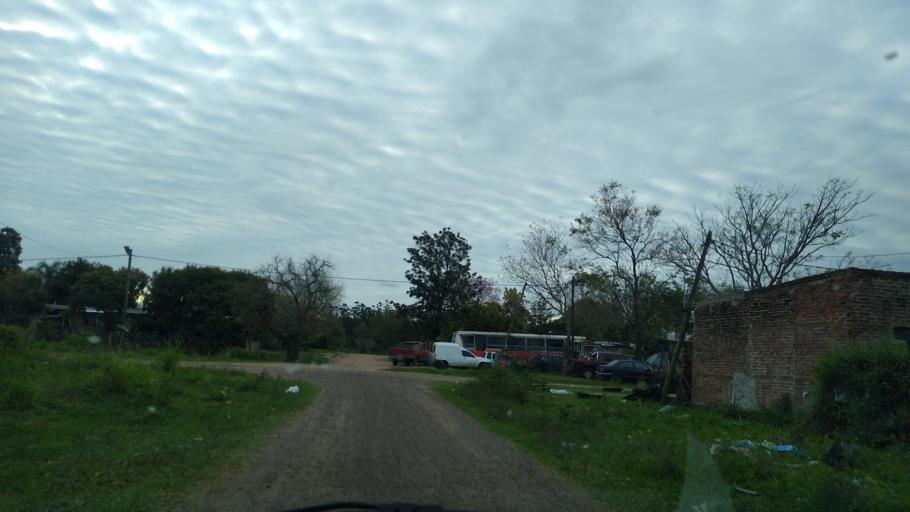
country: AR
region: Chaco
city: Fontana
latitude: -27.4005
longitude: -59.0383
